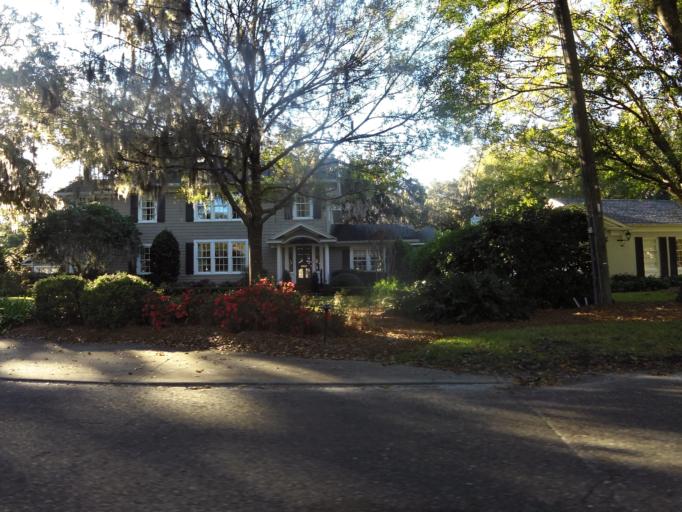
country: US
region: Florida
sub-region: Duval County
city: Jacksonville
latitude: 30.2787
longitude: -81.6983
